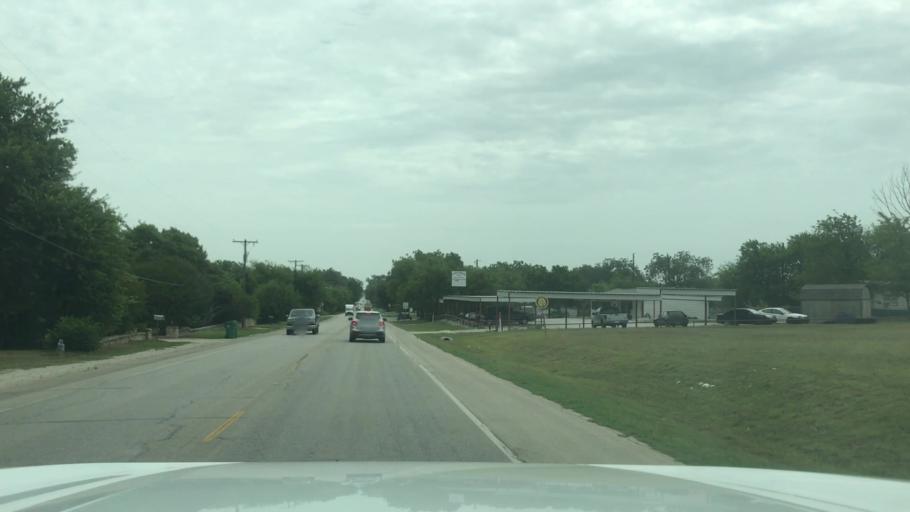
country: US
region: Texas
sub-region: Erath County
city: Dublin
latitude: 32.0876
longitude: -98.3530
